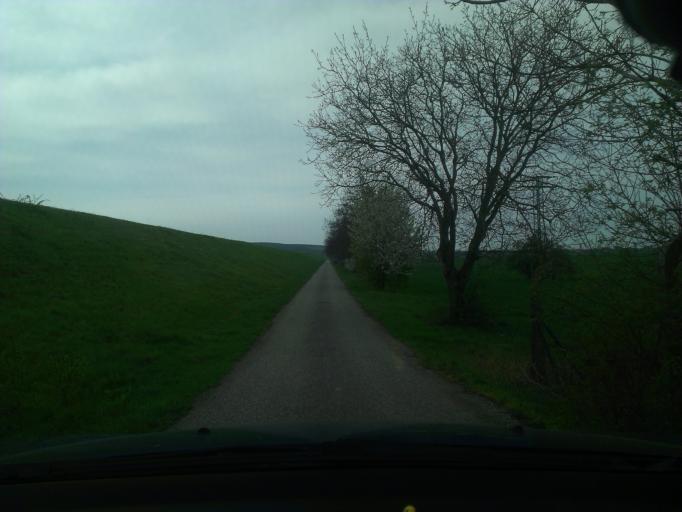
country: SK
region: Trnavsky
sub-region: Okres Trnava
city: Piestany
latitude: 48.5345
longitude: 17.8146
